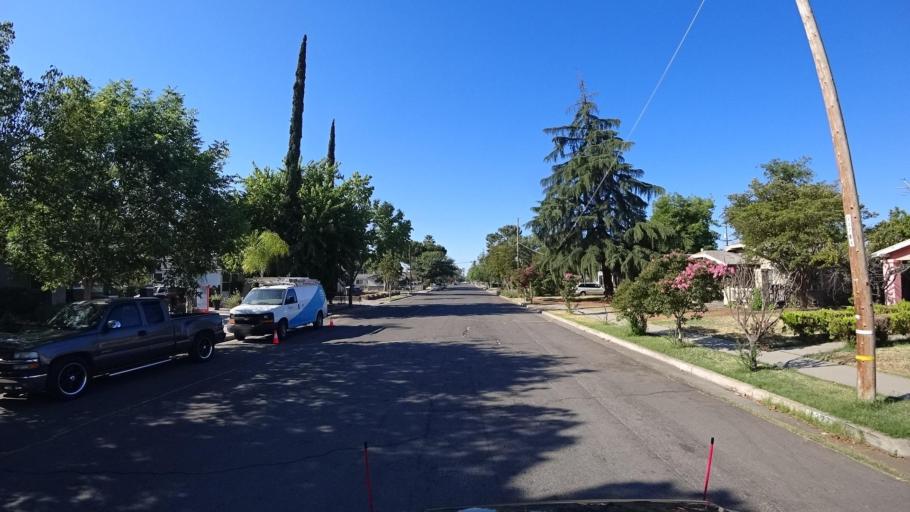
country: US
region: California
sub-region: Fresno County
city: Fresno
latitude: 36.7601
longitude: -119.8131
